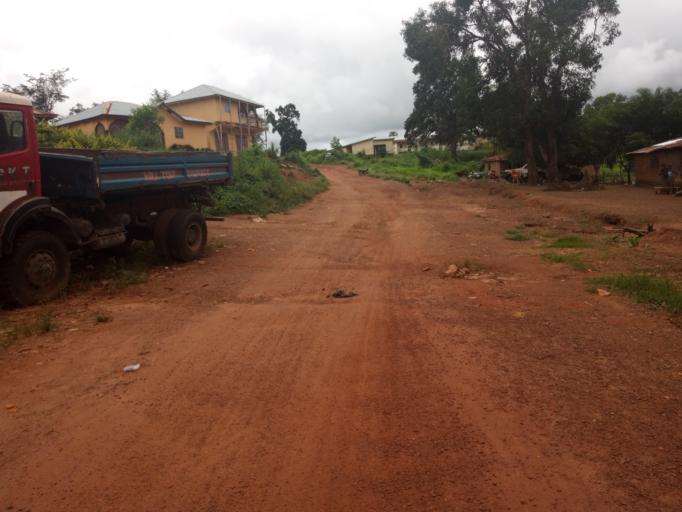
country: SL
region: Northern Province
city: Kamakwie
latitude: 9.5004
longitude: -12.2488
